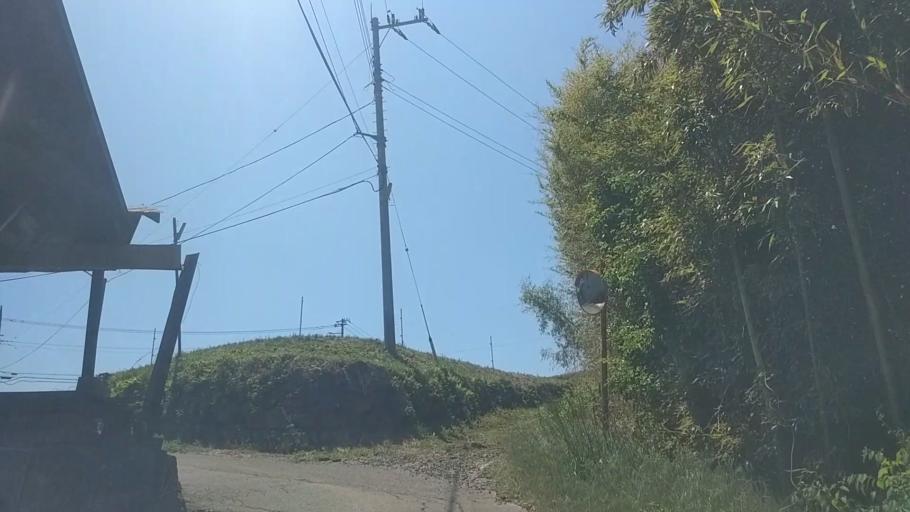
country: JP
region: Yamanashi
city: Nirasaki
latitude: 35.8893
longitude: 138.4587
